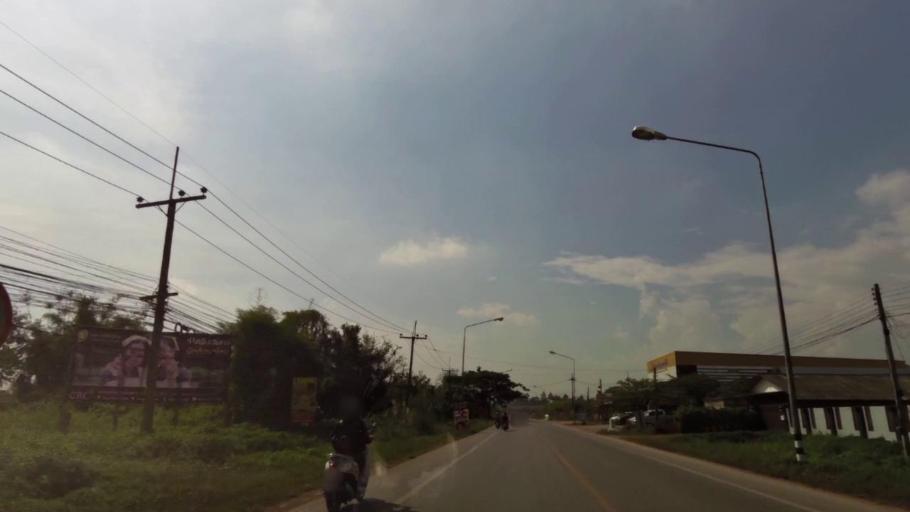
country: TH
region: Chiang Rai
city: Chiang Rai
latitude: 19.8780
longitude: 99.7898
